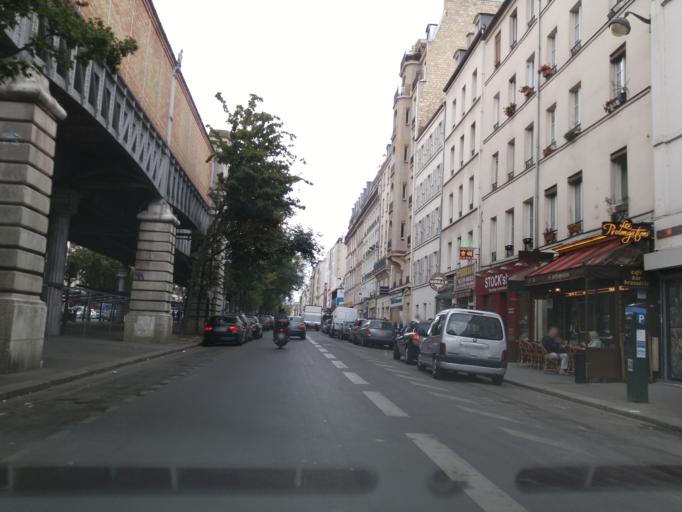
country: FR
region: Ile-de-France
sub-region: Departement des Hauts-de-Seine
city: Vanves
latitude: 48.8503
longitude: 2.2934
